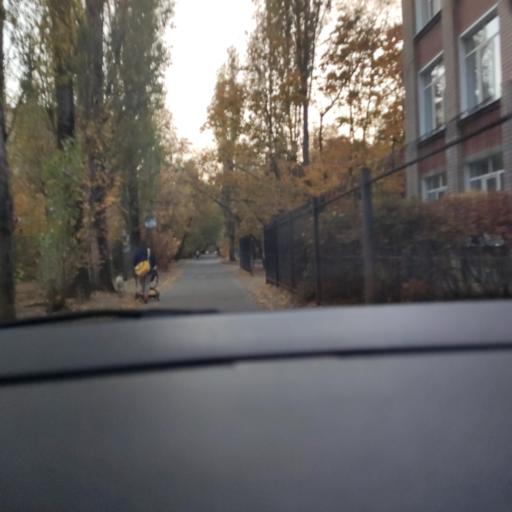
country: RU
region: Voronezj
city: Voronezh
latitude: 51.6529
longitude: 39.1553
